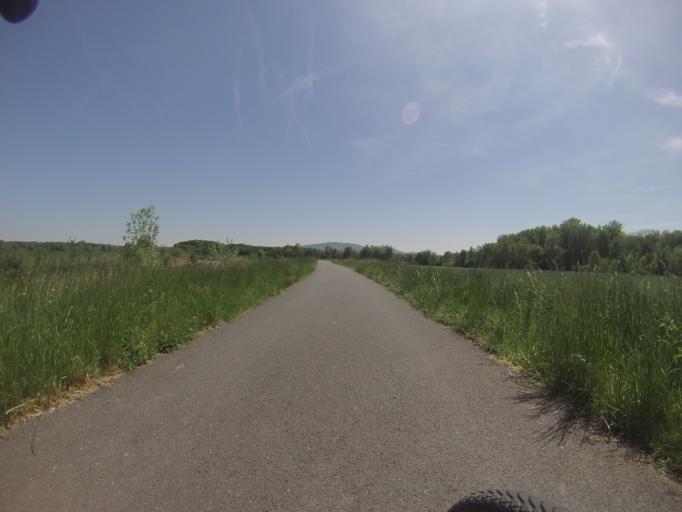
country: CZ
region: South Moravian
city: Vranovice
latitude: 48.9216
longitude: 16.5865
